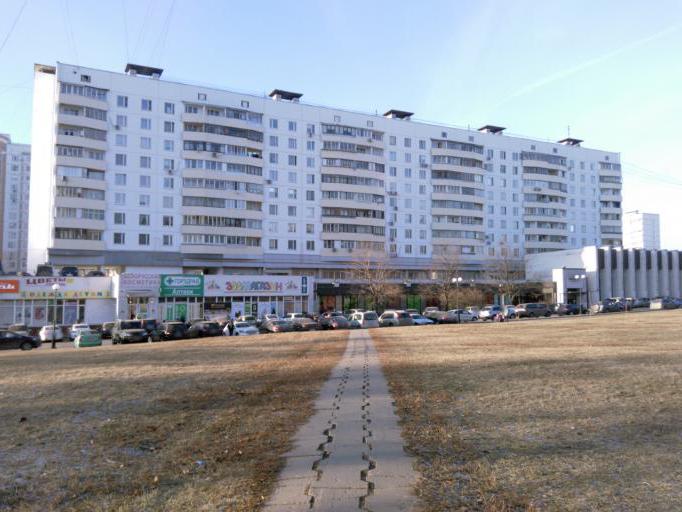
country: RU
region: Moscow
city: Troparevo
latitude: 55.6548
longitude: 37.4859
